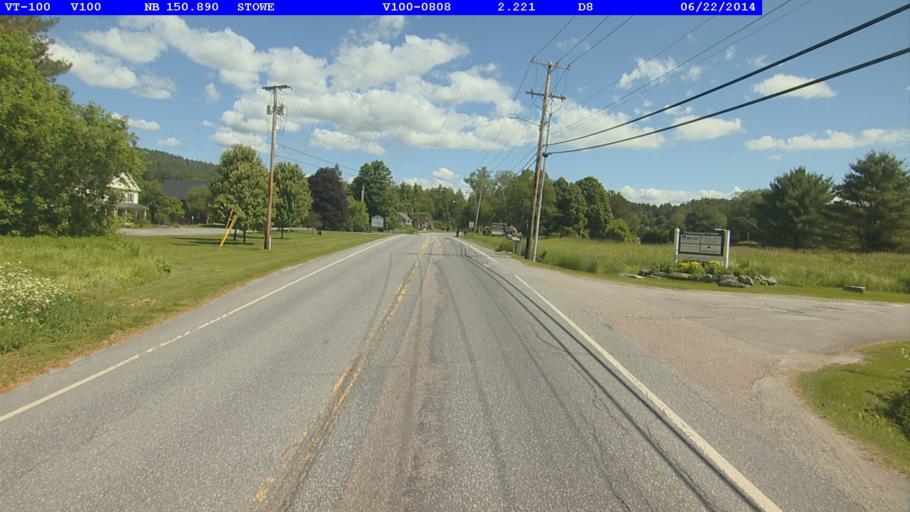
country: US
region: Vermont
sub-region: Lamoille County
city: Morristown
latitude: 44.4520
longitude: -72.6972
